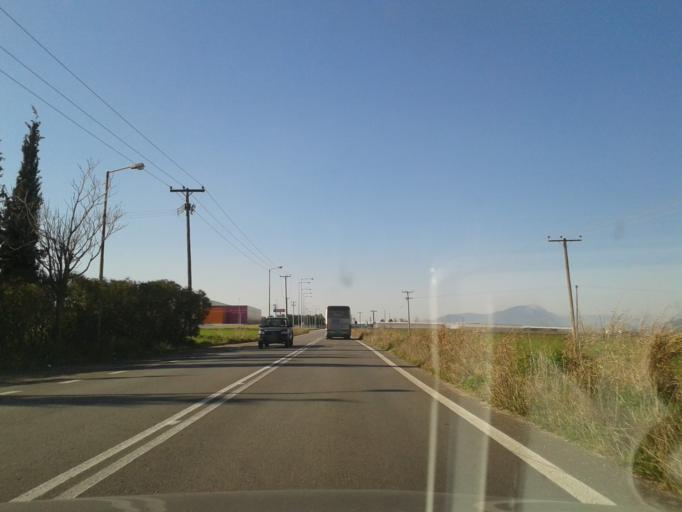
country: GR
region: Central Greece
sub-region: Nomos Voiotias
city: Thivai
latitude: 38.3481
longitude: 23.3730
